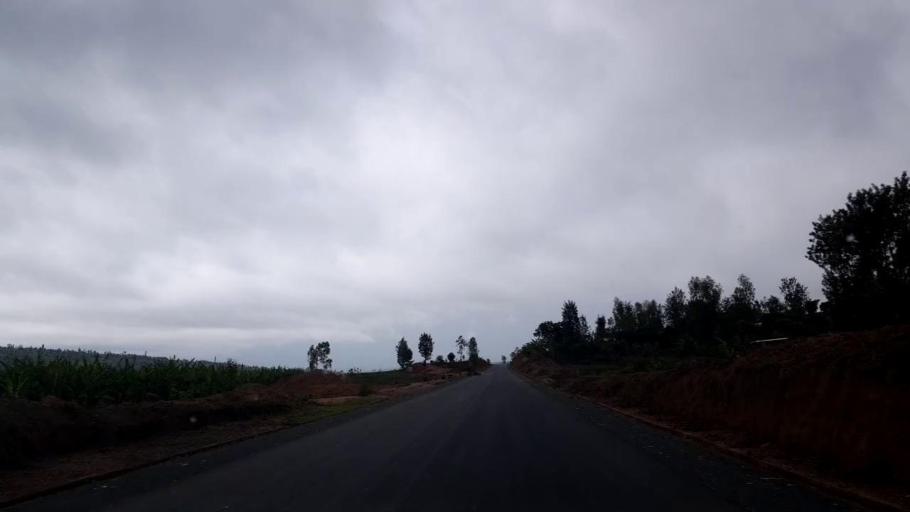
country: RW
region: Northern Province
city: Byumba
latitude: -1.4291
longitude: 30.2643
